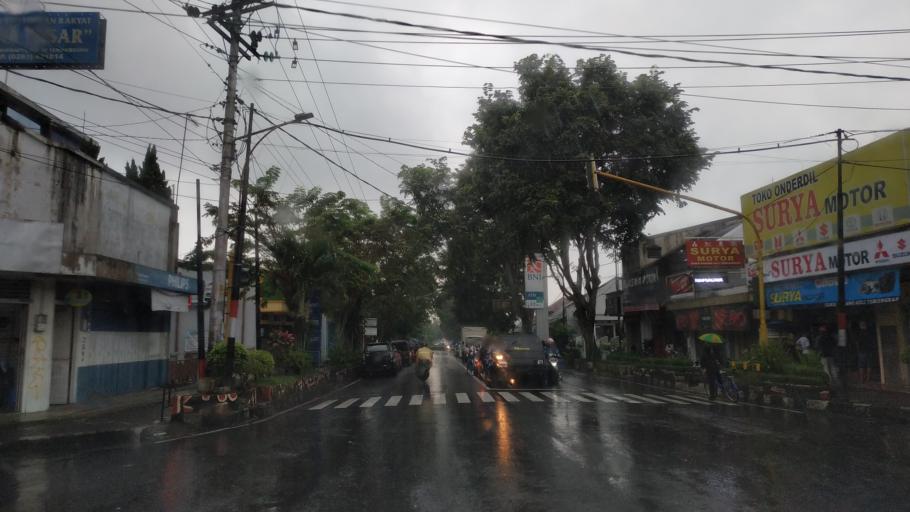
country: ID
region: Central Java
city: Magelang
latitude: -7.3165
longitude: 110.1771
